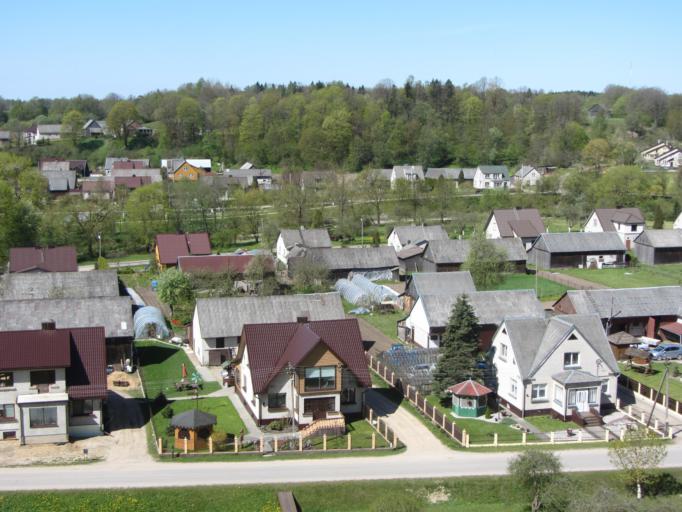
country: LT
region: Taurages apskritis
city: Taurage
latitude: 55.3704
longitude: 22.2351
